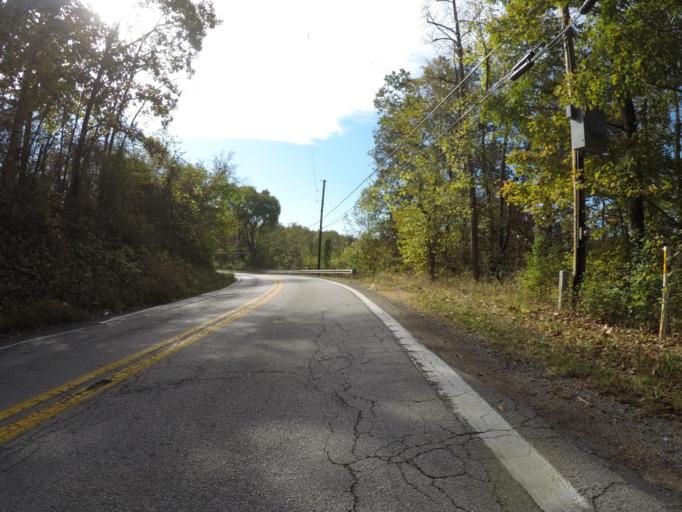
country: US
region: West Virginia
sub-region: Wayne County
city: Ceredo
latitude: 38.3628
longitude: -82.5301
